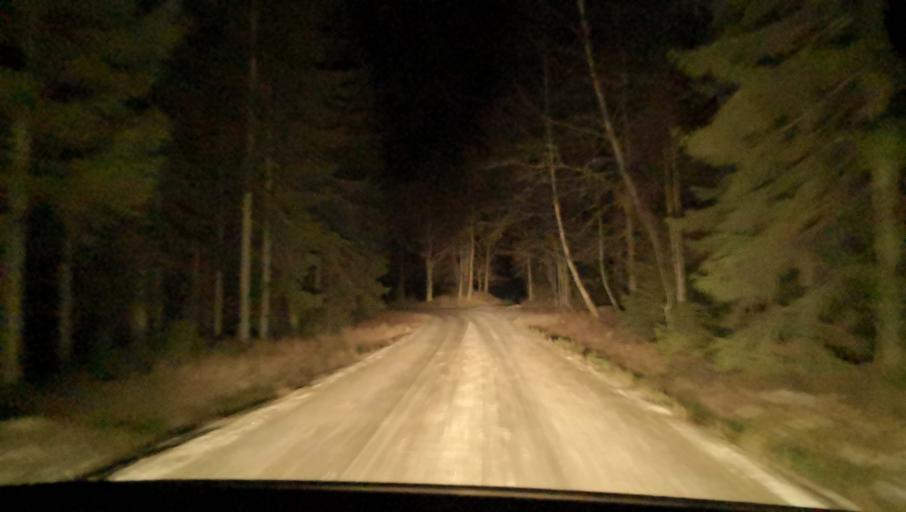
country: SE
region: Stockholm
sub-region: Nacka Kommun
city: Alta
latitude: 59.2854
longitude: 18.2160
